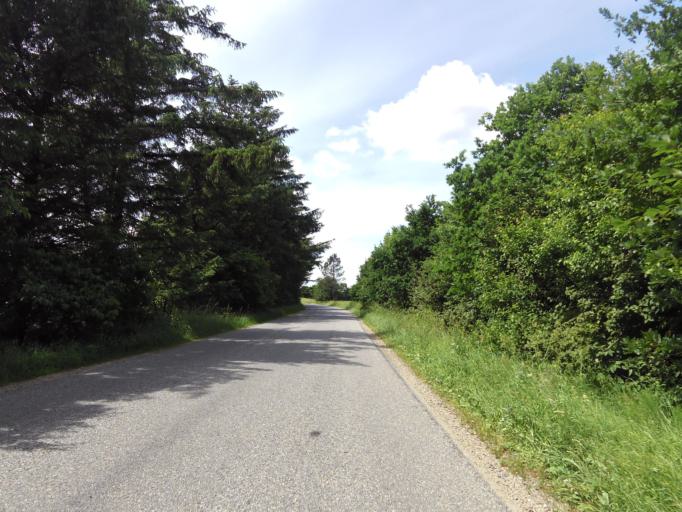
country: DK
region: South Denmark
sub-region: Esbjerg Kommune
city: Ribe
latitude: 55.2626
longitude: 8.8808
